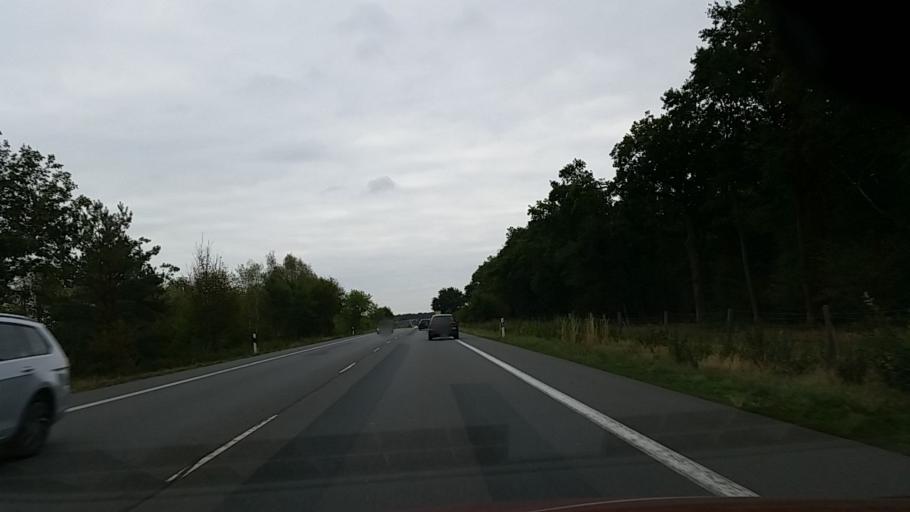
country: DE
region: Lower Saxony
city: Tappenbeck
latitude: 52.4556
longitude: 10.7678
